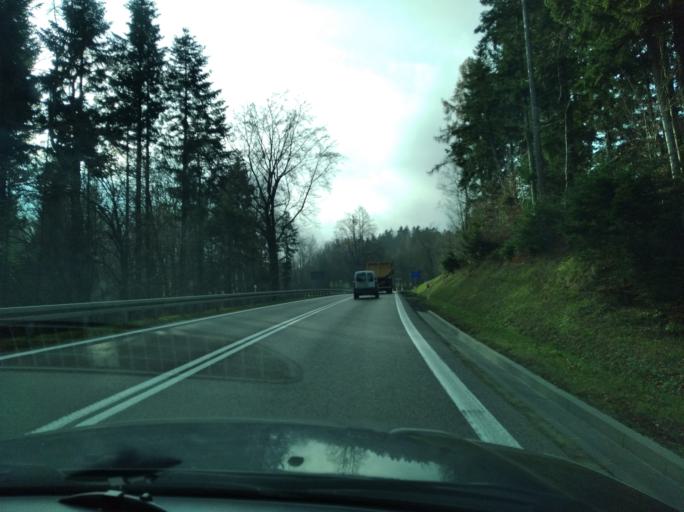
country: PL
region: Subcarpathian Voivodeship
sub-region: Powiat brzozowski
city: Jablonica Polska
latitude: 49.7322
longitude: 21.9077
